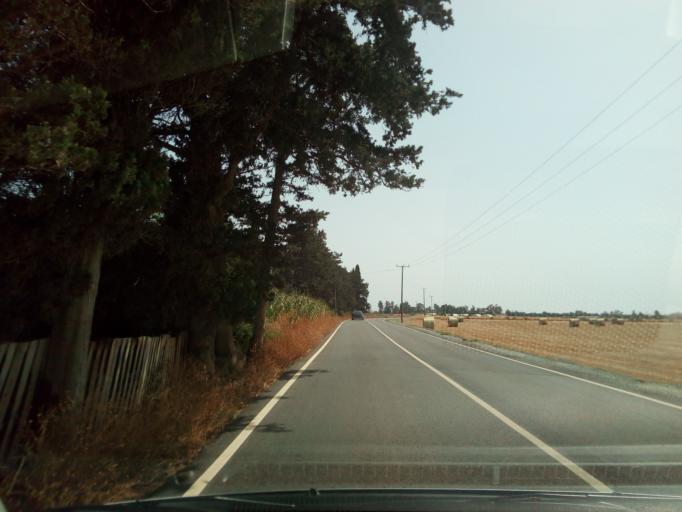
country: CY
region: Larnaka
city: Meneou
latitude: 34.8457
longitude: 33.5937
